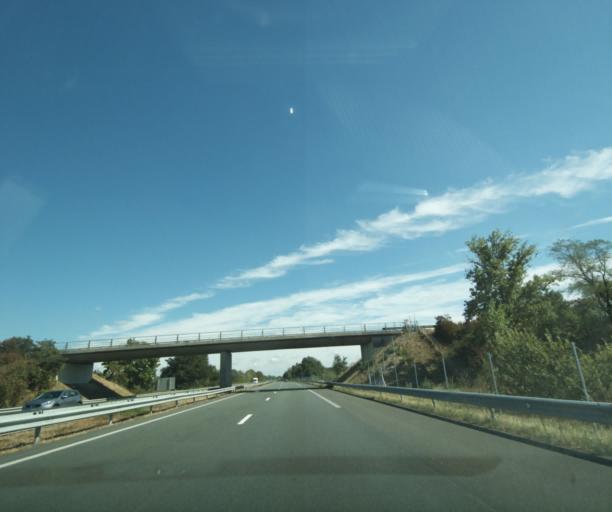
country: FR
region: Aquitaine
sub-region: Departement du Lot-et-Garonne
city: Sainte-Colombe-en-Bruilhois
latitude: 44.1869
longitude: 0.5361
